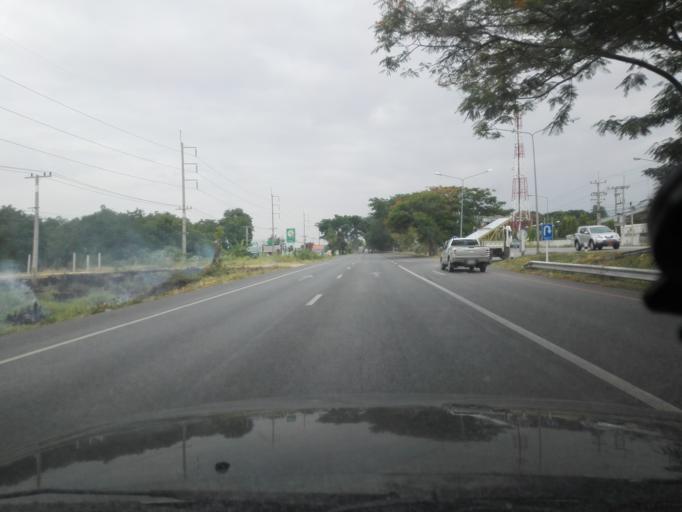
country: TH
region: Nakhon Sawan
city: Nakhon Sawan
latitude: 15.7340
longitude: 100.0275
